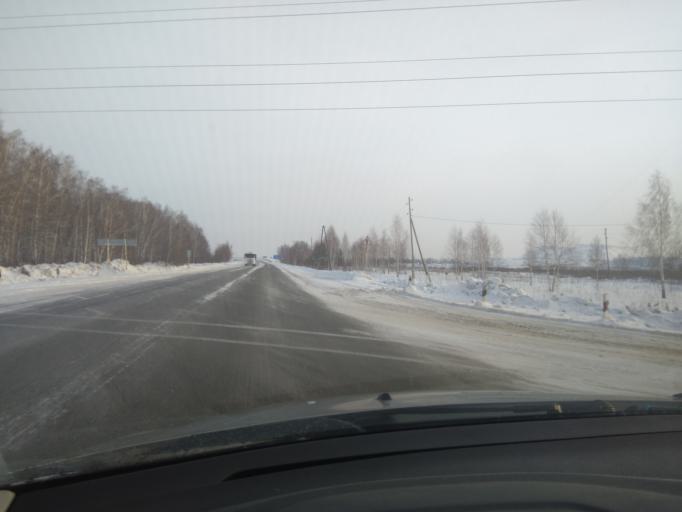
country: RU
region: Sverdlovsk
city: Bogdanovich
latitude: 56.8075
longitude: 62.0334
